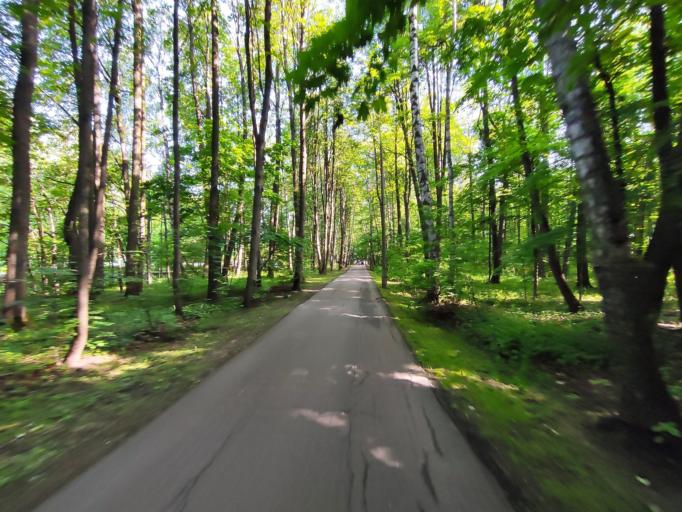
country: RU
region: Moscow
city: Metrogorodok
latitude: 55.7833
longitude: 37.7528
